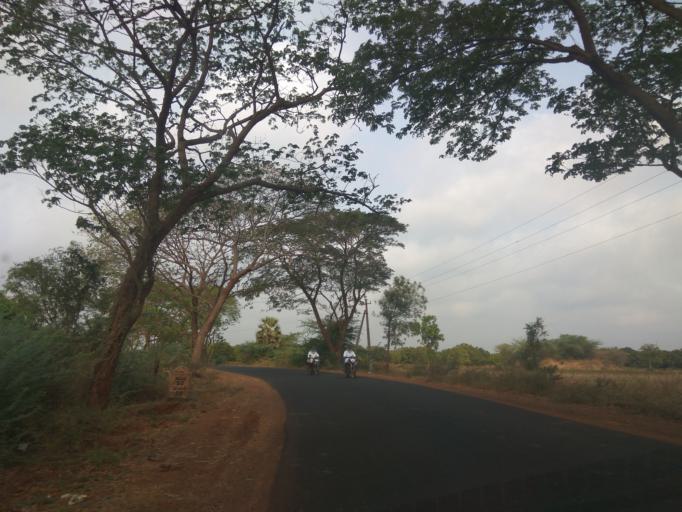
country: IN
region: Andhra Pradesh
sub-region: Prakasam
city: Kandukur
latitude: 15.2050
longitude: 79.8552
